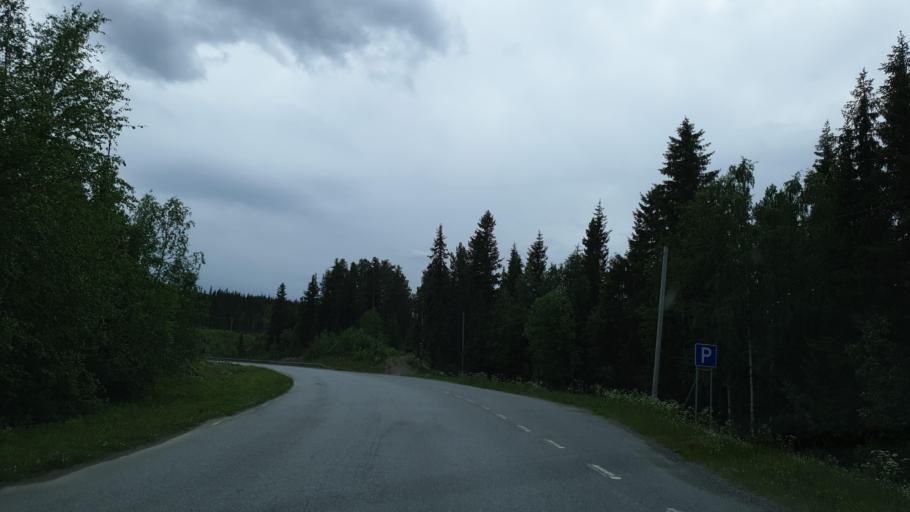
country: SE
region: Vaesterbotten
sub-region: Storumans Kommun
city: Fristad
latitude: 65.4259
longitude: 16.1718
